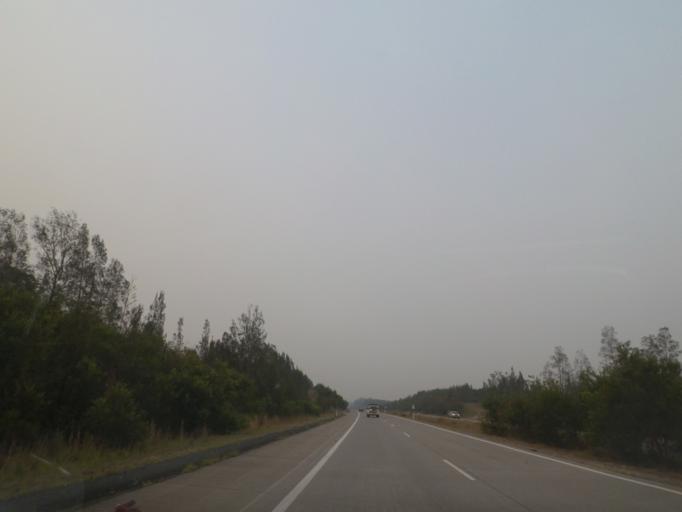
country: AU
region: New South Wales
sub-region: Kempsey
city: Frederickton
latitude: -30.9437
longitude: 152.8644
